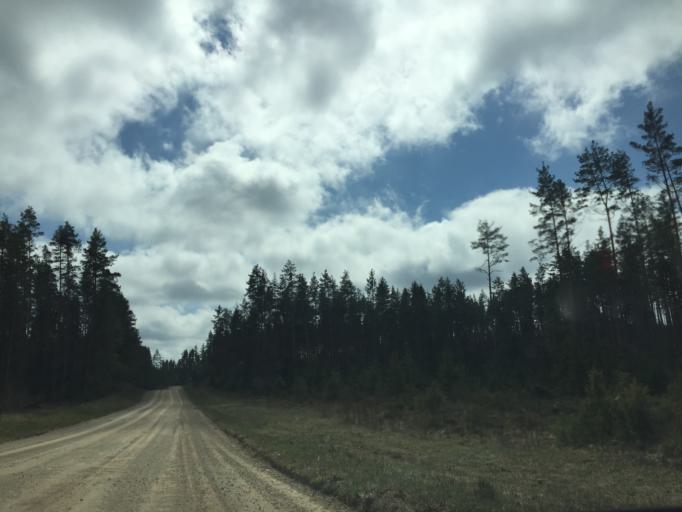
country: EE
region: Valgamaa
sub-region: Valga linn
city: Valga
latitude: 57.6413
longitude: 26.2309
